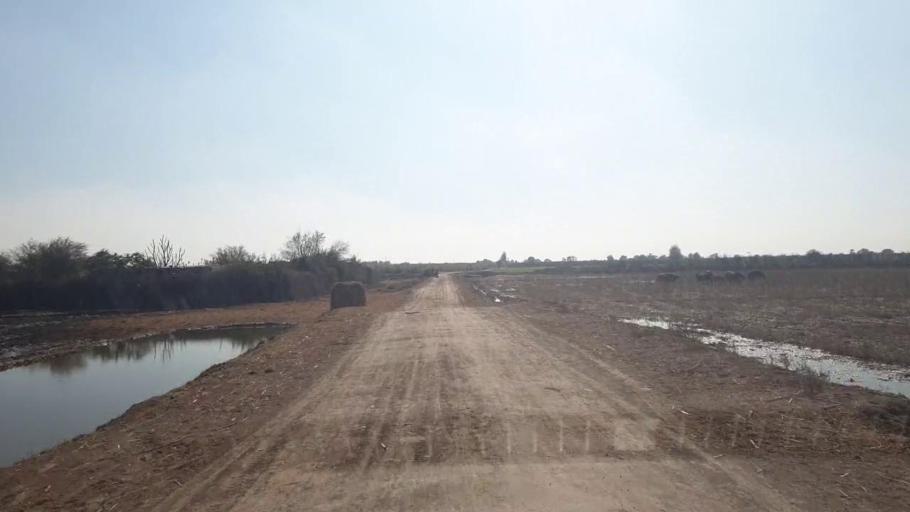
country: PK
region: Sindh
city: Shahdadpur
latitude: 25.8994
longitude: 68.5512
